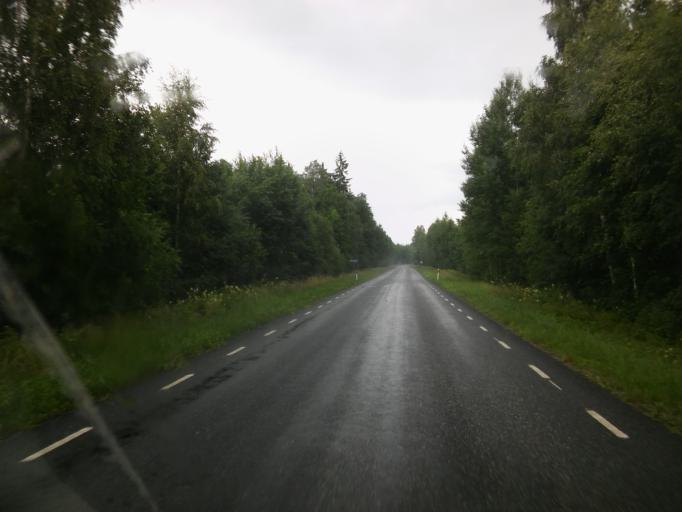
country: EE
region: Paernumaa
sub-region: Halinga vald
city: Parnu-Jaagupi
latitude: 58.7885
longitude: 24.6016
